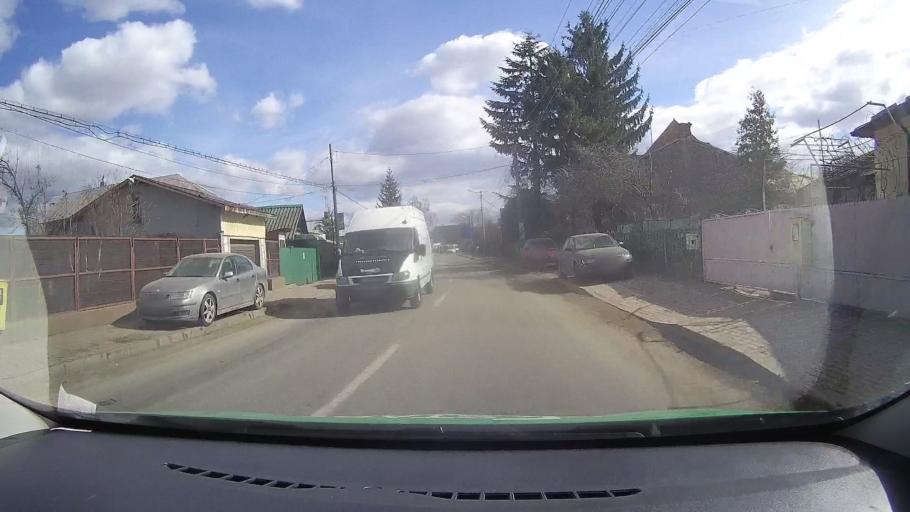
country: RO
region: Dambovita
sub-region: Municipiul Targoviste
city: Targoviste
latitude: 44.9407
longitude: 25.4418
